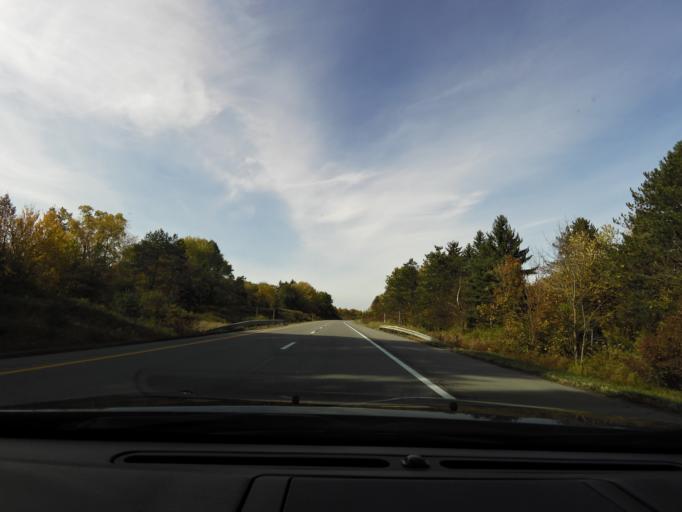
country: US
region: New York
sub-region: Erie County
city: Elma Center
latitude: 42.8158
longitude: -78.6568
